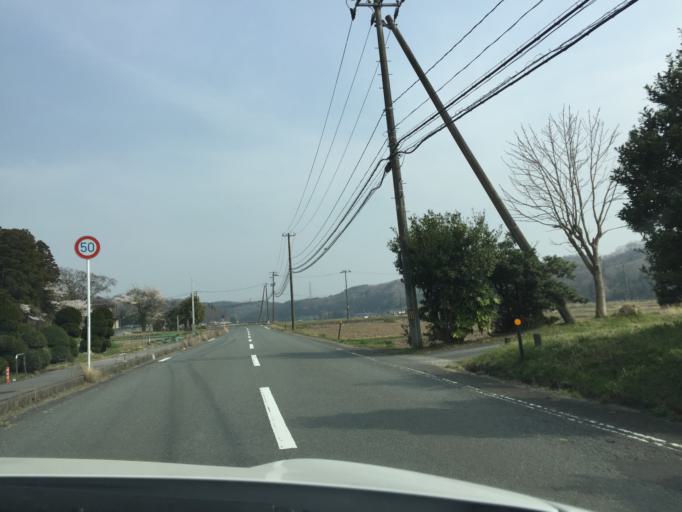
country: JP
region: Fukushima
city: Iwaki
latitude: 36.9640
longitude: 140.8119
